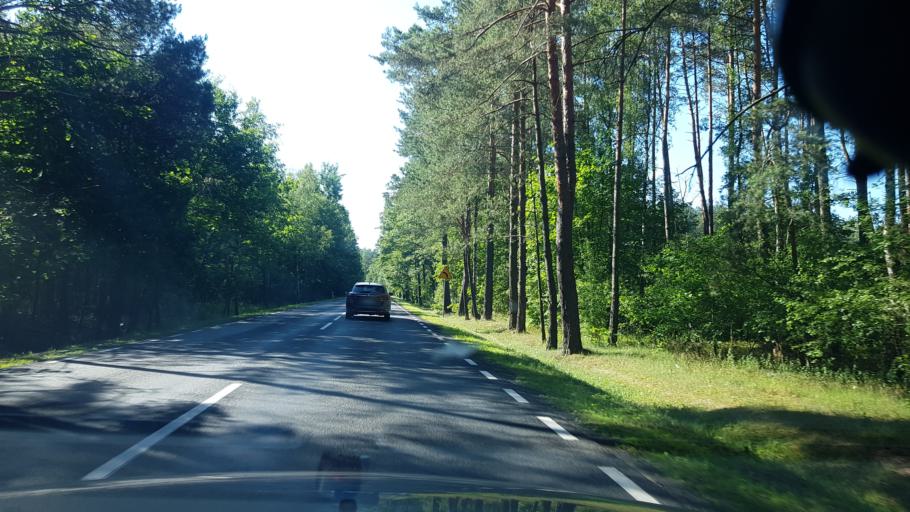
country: PL
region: Masovian Voivodeship
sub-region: Powiat wyszkowski
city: Branszczyk
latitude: 52.5723
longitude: 21.5412
